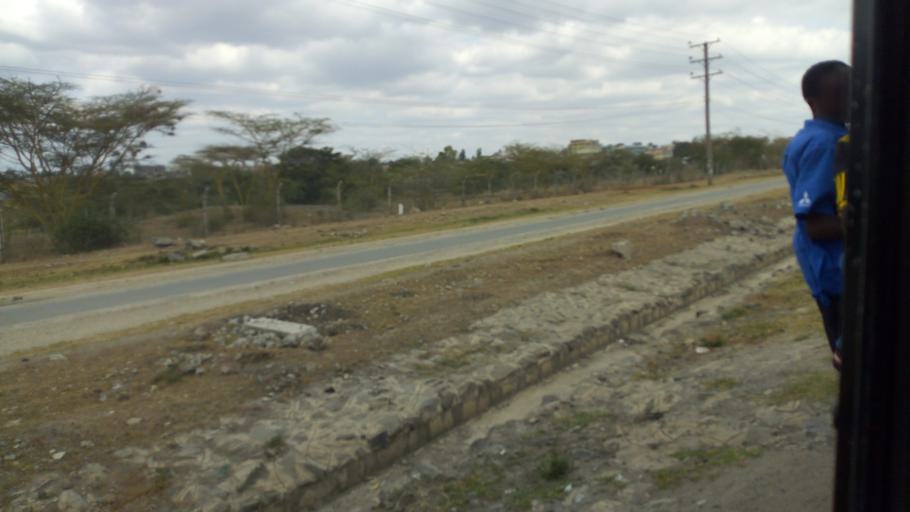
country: KE
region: Machakos
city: Athi River
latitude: -1.4664
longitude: 36.9617
